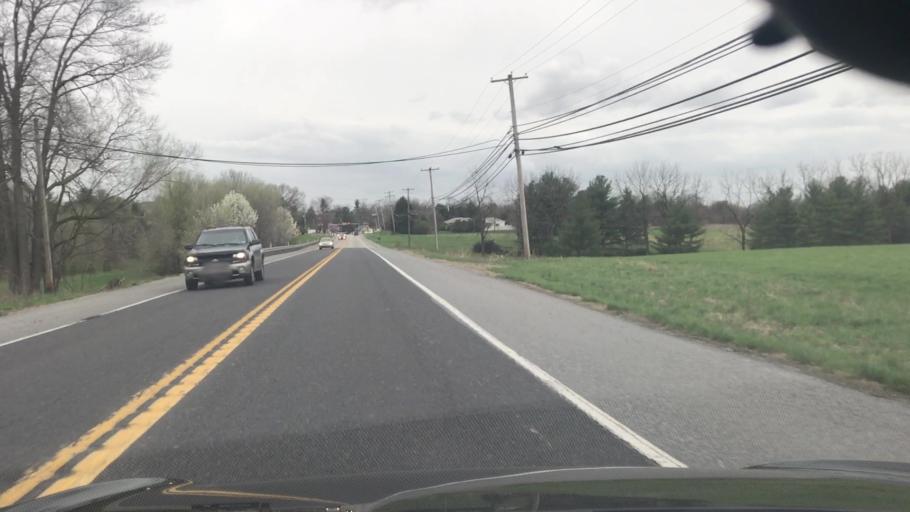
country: US
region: Pennsylvania
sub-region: Cumberland County
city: Mechanicsburg
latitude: 40.2384
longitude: -77.0314
